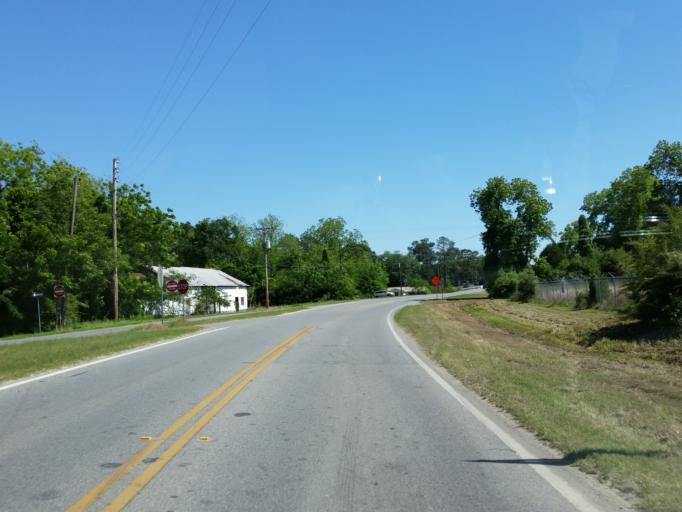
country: US
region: Georgia
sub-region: Cook County
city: Sparks
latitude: 31.1537
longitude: -83.4288
